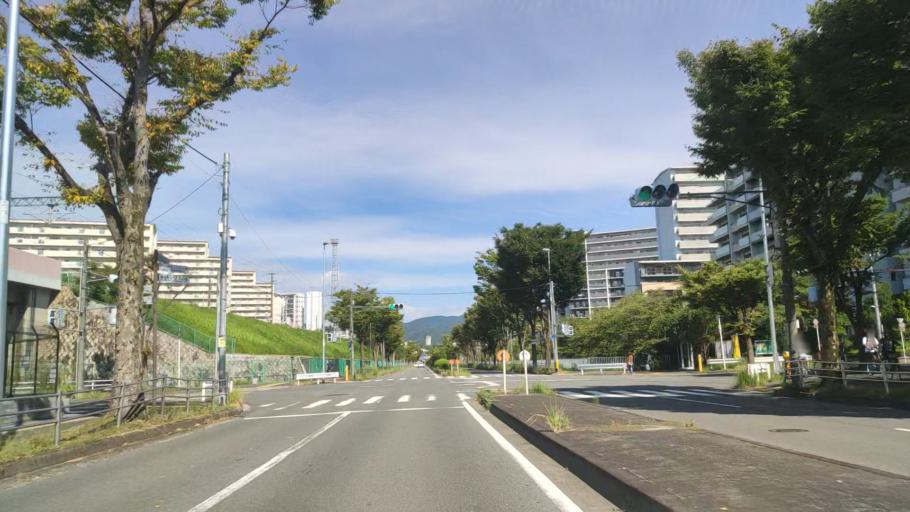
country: JP
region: Osaka
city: Mino
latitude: 34.8156
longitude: 135.5136
